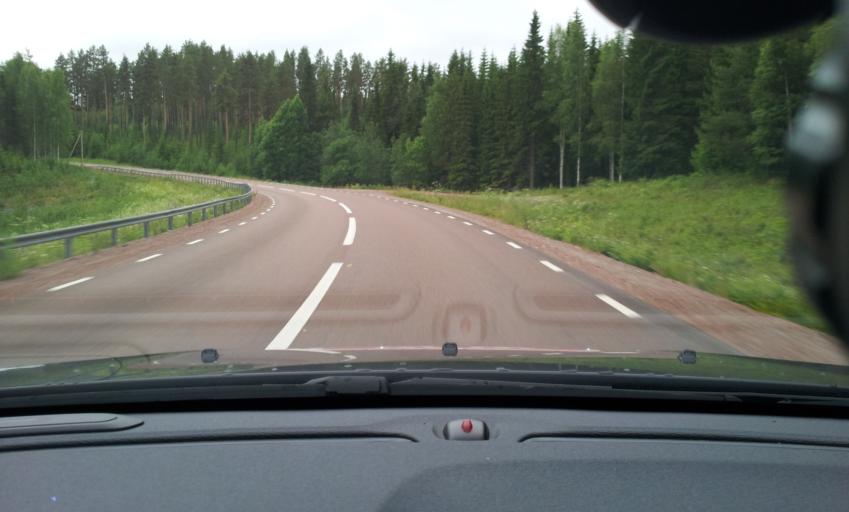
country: SE
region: Jaemtland
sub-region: Ragunda Kommun
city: Hammarstrand
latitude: 63.0369
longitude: 16.5180
